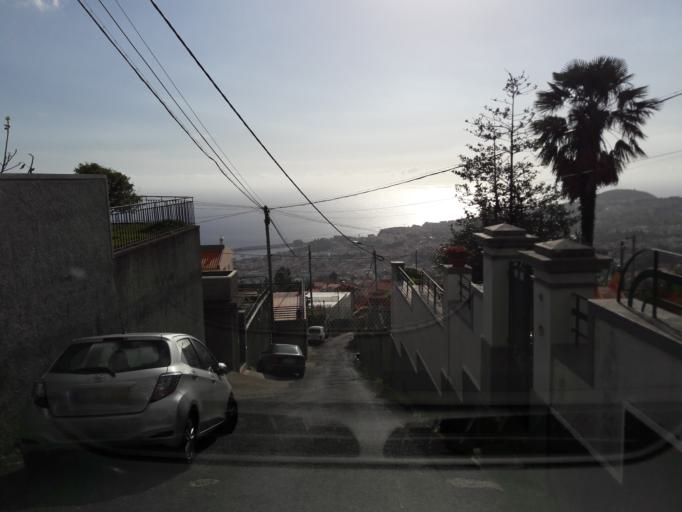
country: PT
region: Madeira
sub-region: Funchal
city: Nossa Senhora do Monte
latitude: 32.6689
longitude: -16.9060
